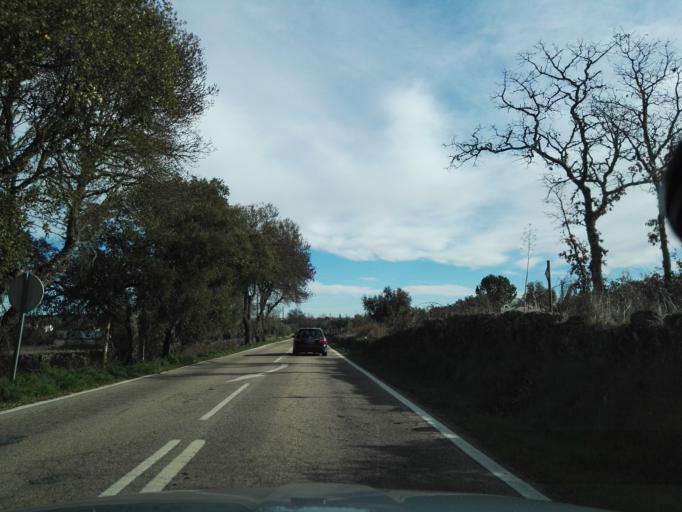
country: PT
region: Portalegre
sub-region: Nisa
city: Nisa
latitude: 39.5031
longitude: -7.6704
